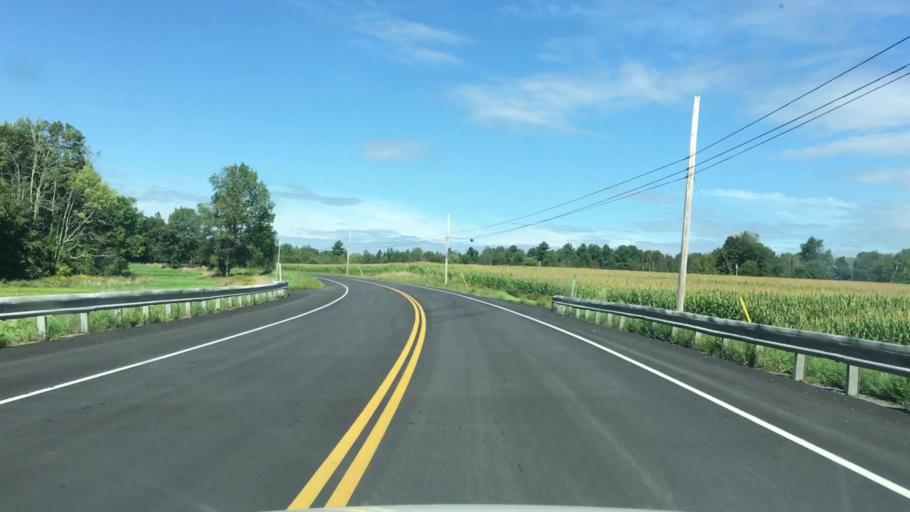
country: US
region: Maine
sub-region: Penobscot County
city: Corinna
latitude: 44.9488
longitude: -69.2475
